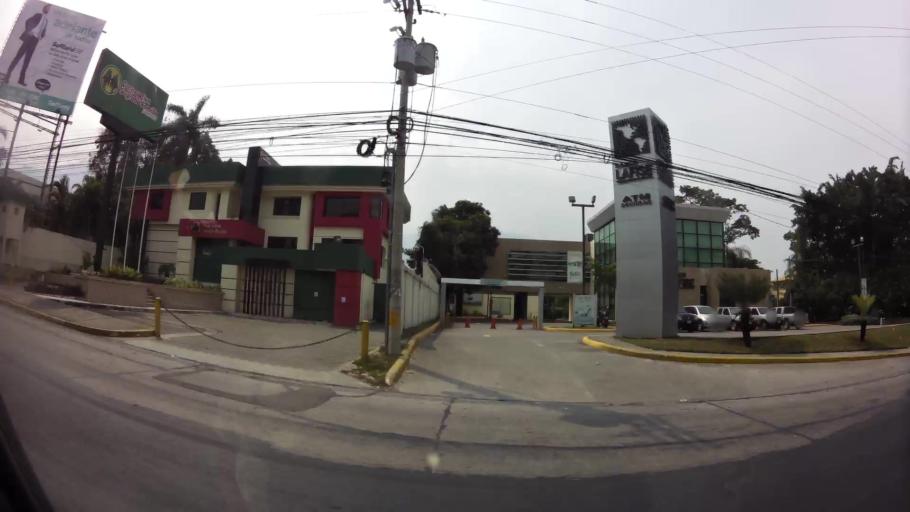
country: HN
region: Cortes
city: San Pedro Sula
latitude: 15.5141
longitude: -88.0352
